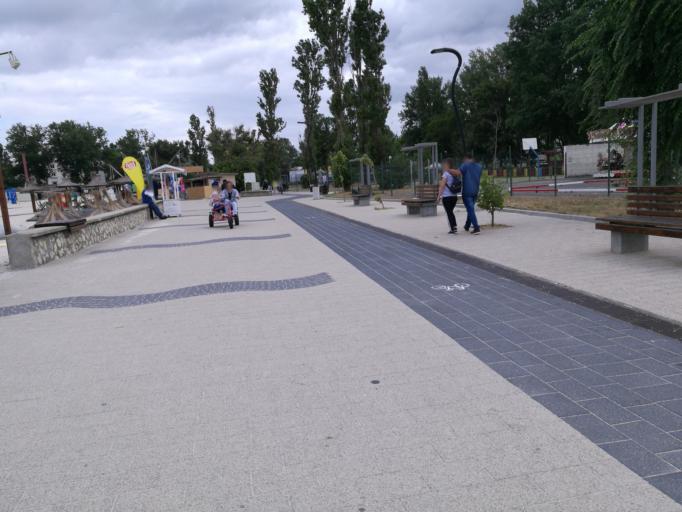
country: RO
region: Constanta
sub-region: Municipiul Constanta
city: Palazu Mare
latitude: 44.2507
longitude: 28.6221
